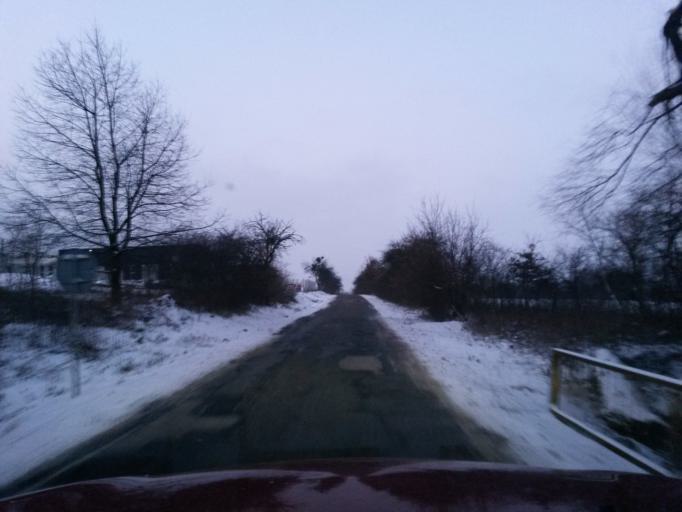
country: SK
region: Kosicky
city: Kosice
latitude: 48.7368
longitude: 21.3263
